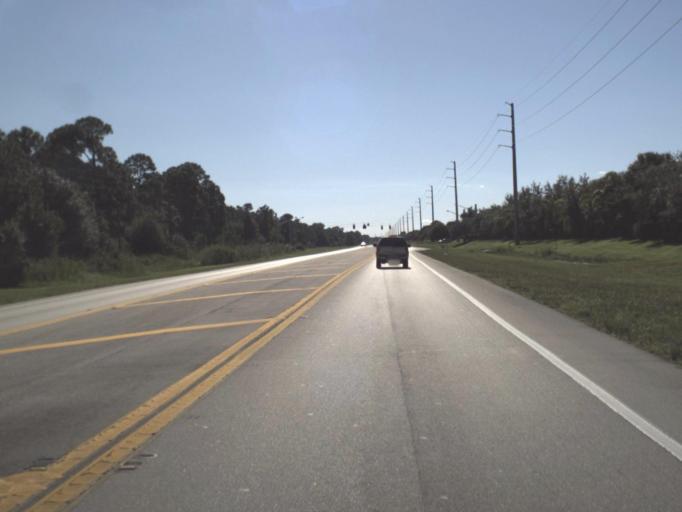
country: US
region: Florida
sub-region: Lee County
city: Gateway
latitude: 26.6103
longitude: -81.7583
